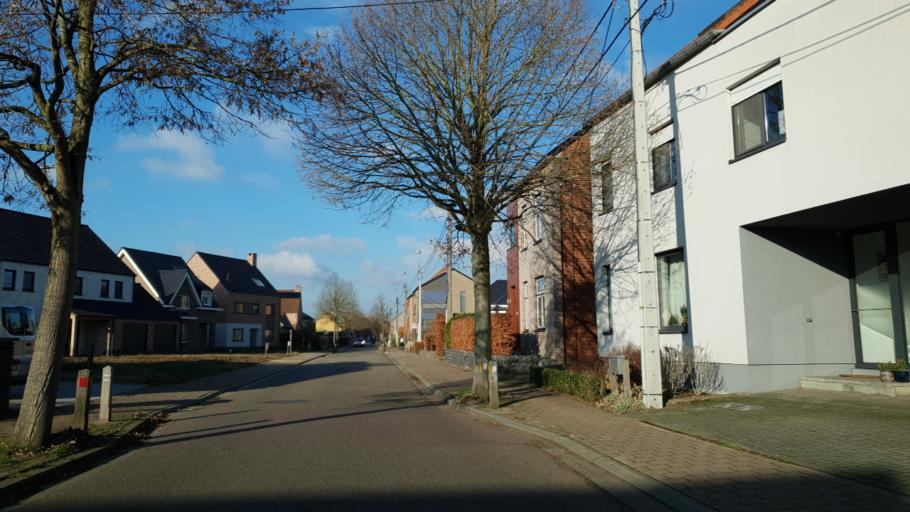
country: BE
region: Flanders
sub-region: Provincie Vlaams-Brabant
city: Herent
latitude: 50.9179
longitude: 4.6834
